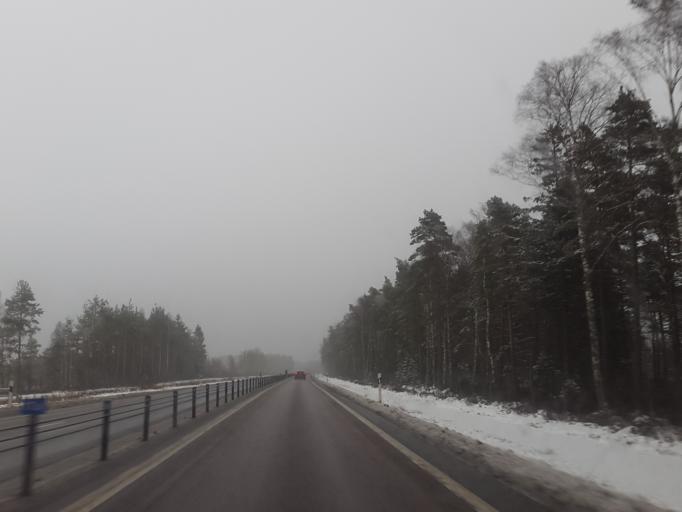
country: SE
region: Joenkoeping
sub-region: Jonkopings Kommun
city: Taberg
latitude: 57.7672
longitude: 14.0281
